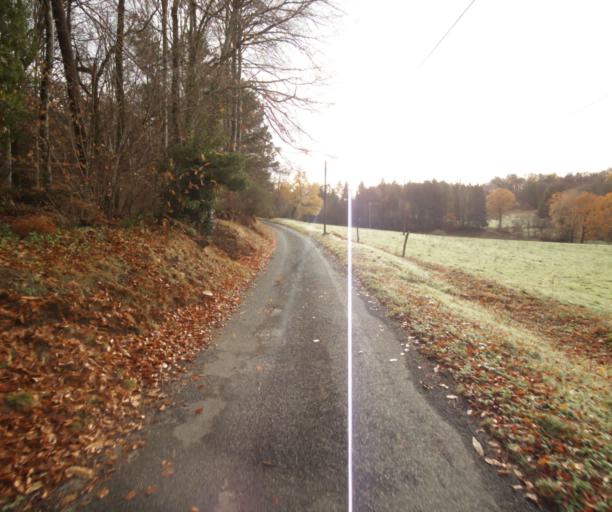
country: FR
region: Limousin
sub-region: Departement de la Correze
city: Cornil
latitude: 45.1980
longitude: 1.7137
